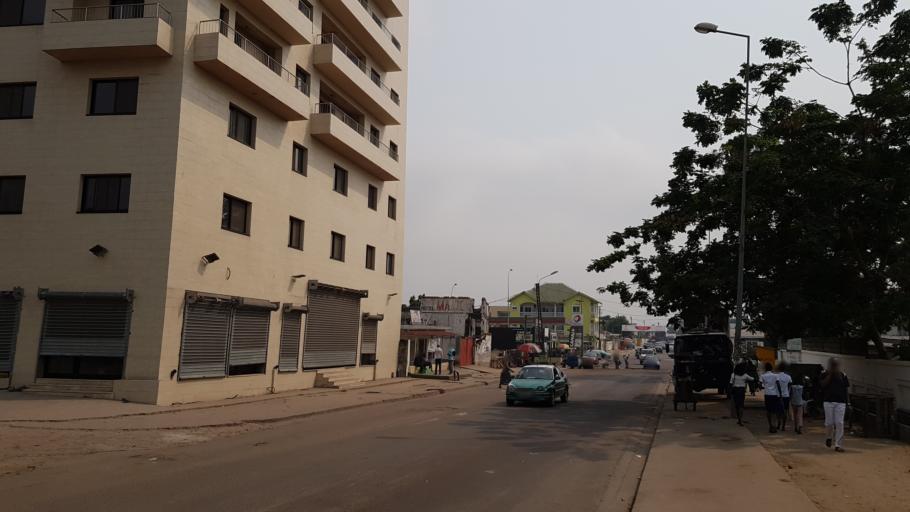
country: CG
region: Brazzaville
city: Brazzaville
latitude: -4.2627
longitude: 15.2607
